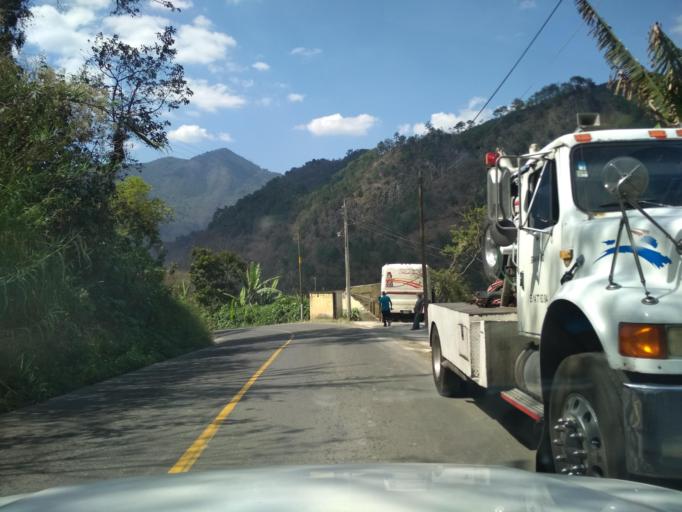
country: MX
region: Veracruz
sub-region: Tlilapan
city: Tonalixco
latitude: 18.7850
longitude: -97.0901
